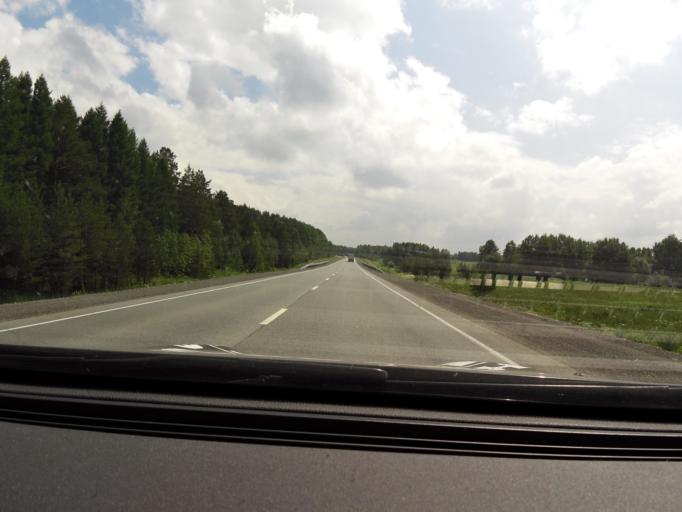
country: RU
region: Perm
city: Suksun
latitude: 57.0043
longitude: 57.4762
